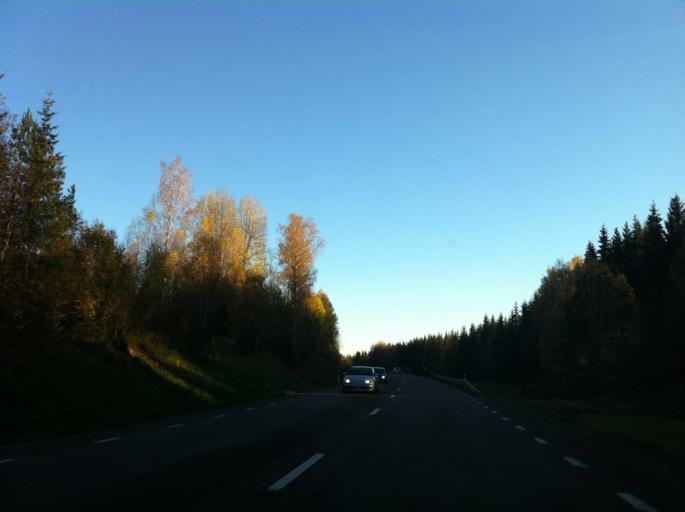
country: SE
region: Dalarna
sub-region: Faluns Kommun
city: Falun
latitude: 60.6538
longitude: 15.5566
